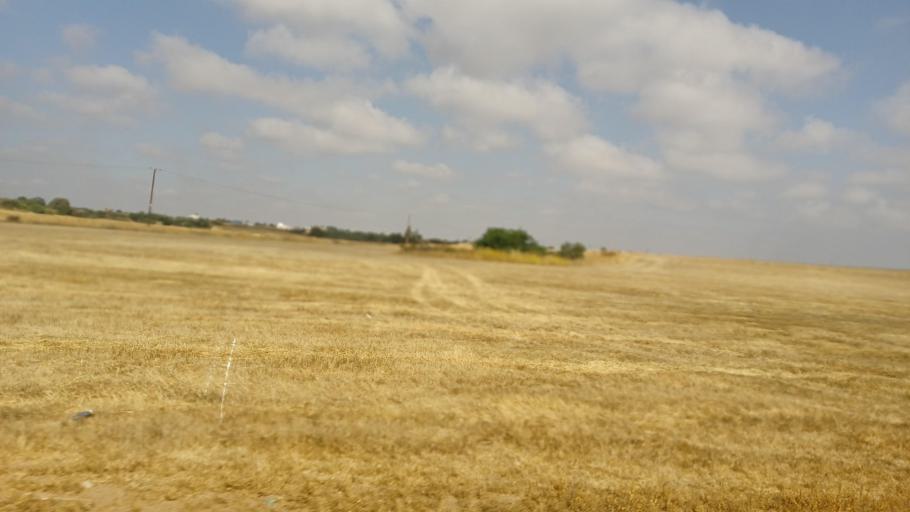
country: CY
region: Ammochostos
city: Paralimni
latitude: 35.0194
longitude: 34.0010
